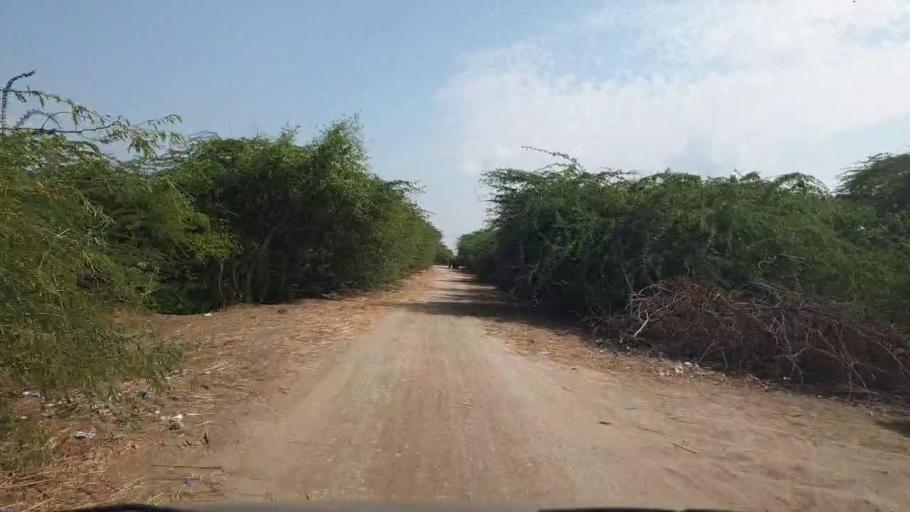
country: PK
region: Sindh
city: Badin
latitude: 24.4658
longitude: 68.5850
